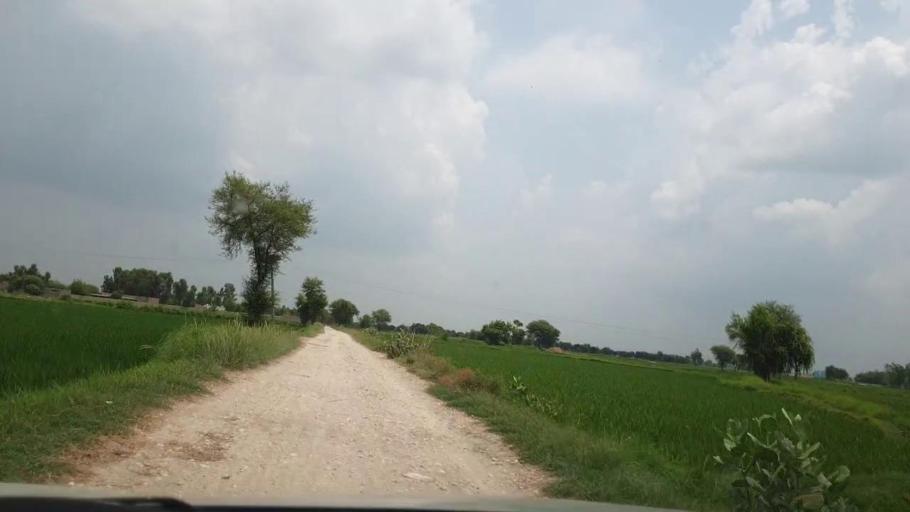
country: PK
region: Sindh
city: Goth Garelo
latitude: 27.4249
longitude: 68.0809
